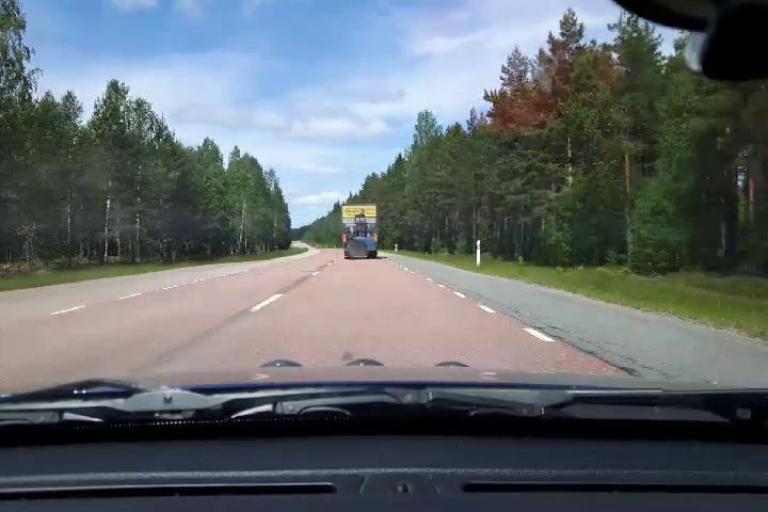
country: SE
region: Uppsala
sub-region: Osthammars Kommun
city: Bjorklinge
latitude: 60.1316
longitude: 17.5092
